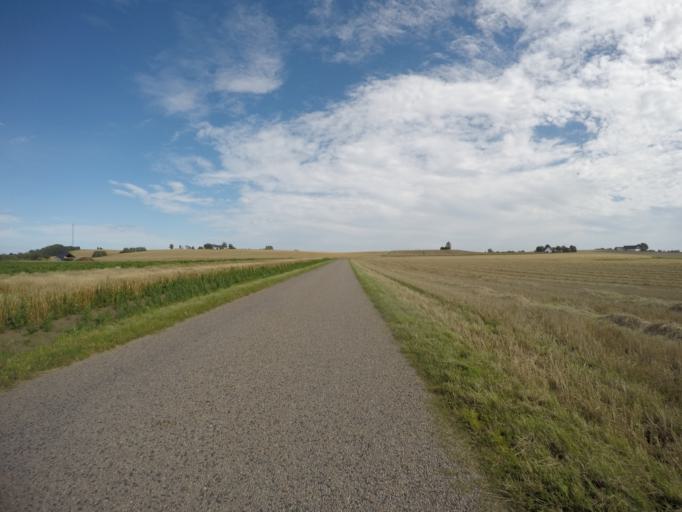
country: SE
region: Skane
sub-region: Simrishamns Kommun
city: Simrishamn
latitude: 55.4959
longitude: 14.2407
